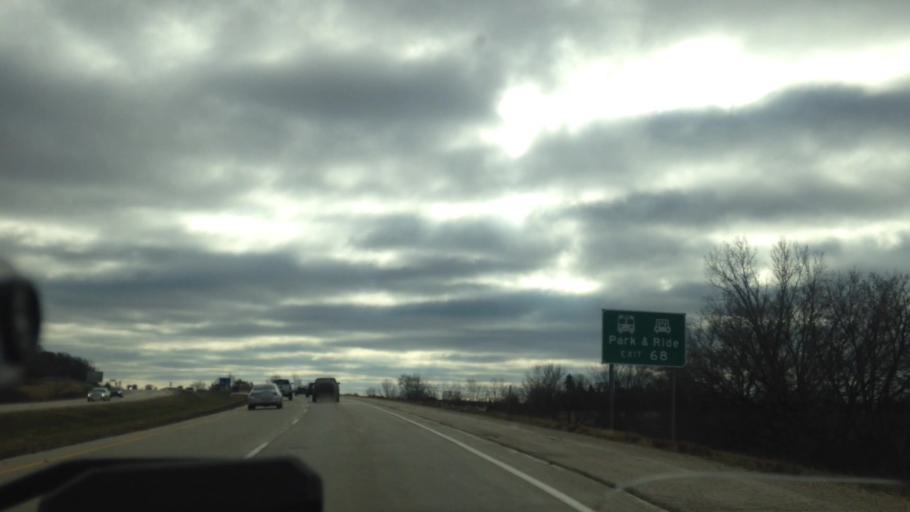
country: US
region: Wisconsin
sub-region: Washington County
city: West Bend
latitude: 43.4096
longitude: -88.2037
